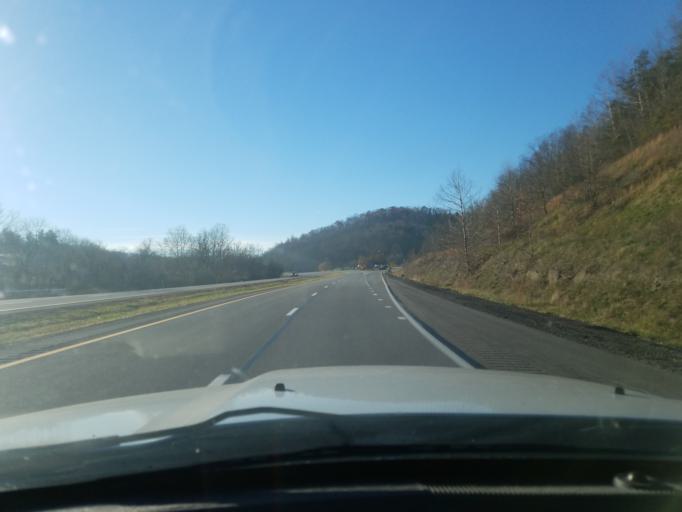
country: US
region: West Virginia
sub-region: Wood County
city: Mineral Wells
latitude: 39.1363
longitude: -81.5488
